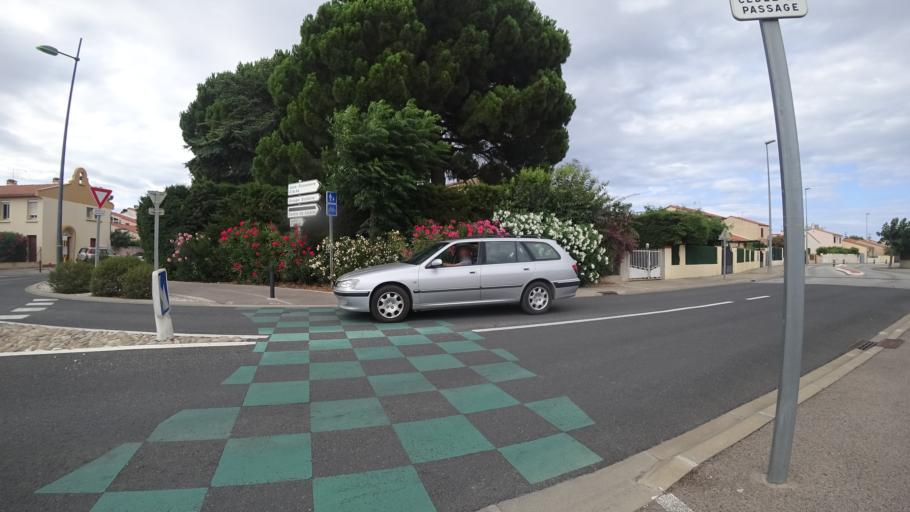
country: FR
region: Languedoc-Roussillon
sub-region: Departement des Pyrenees-Orientales
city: Saint-Laurent-de-la-Salanque
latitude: 42.7676
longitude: 2.9872
